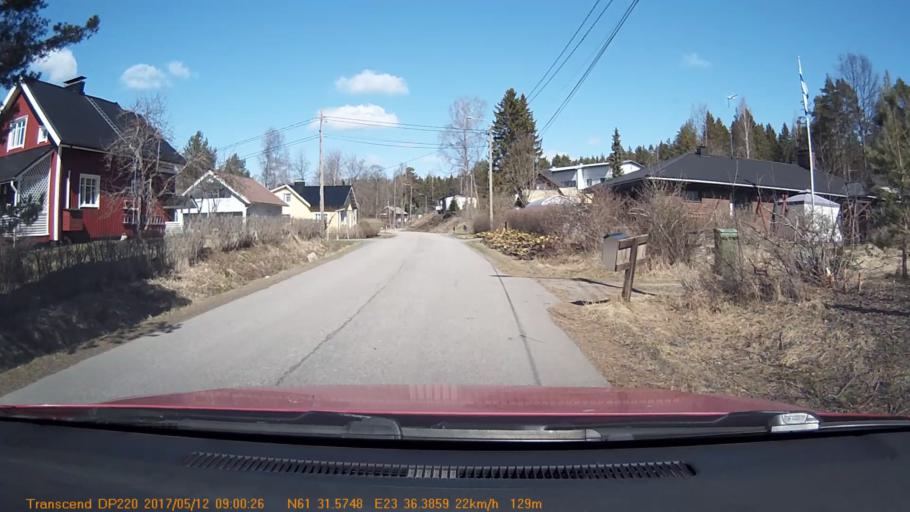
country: FI
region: Pirkanmaa
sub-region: Tampere
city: Yloejaervi
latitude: 61.5263
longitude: 23.6063
